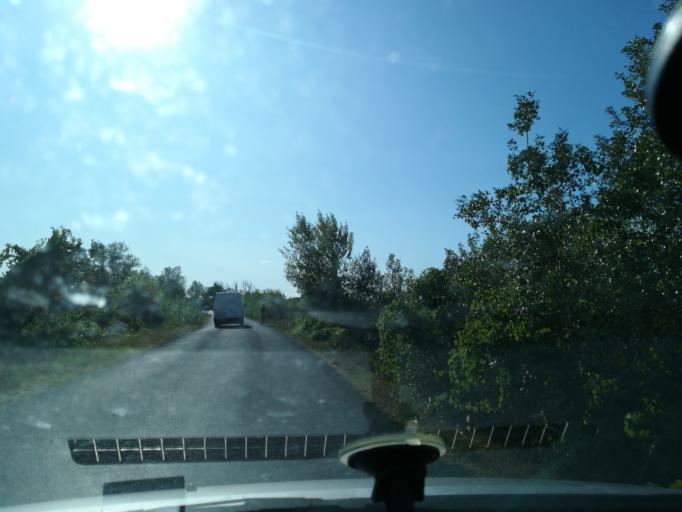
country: FR
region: Languedoc-Roussillon
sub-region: Departement de l'Herault
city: Vias
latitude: 43.2911
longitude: 3.3862
